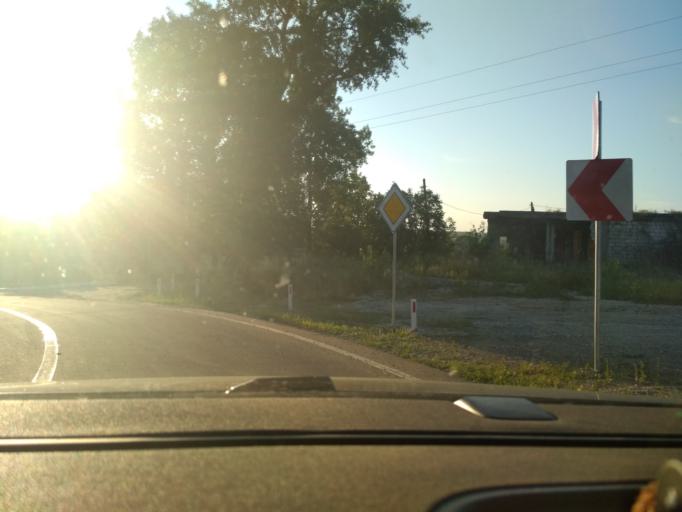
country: RO
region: Iasi
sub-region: Comuna Grozesti
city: Grozesti
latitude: 46.9678
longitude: 28.1143
